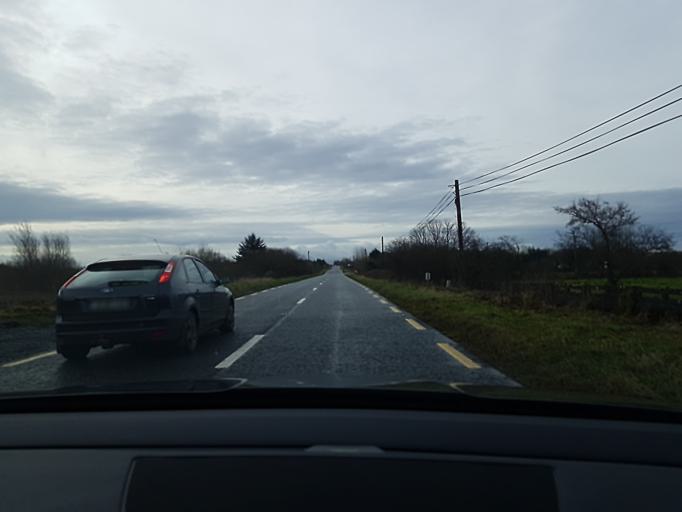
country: IE
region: Connaught
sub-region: Maigh Eo
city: Castlebar
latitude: 53.8257
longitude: -9.3076
